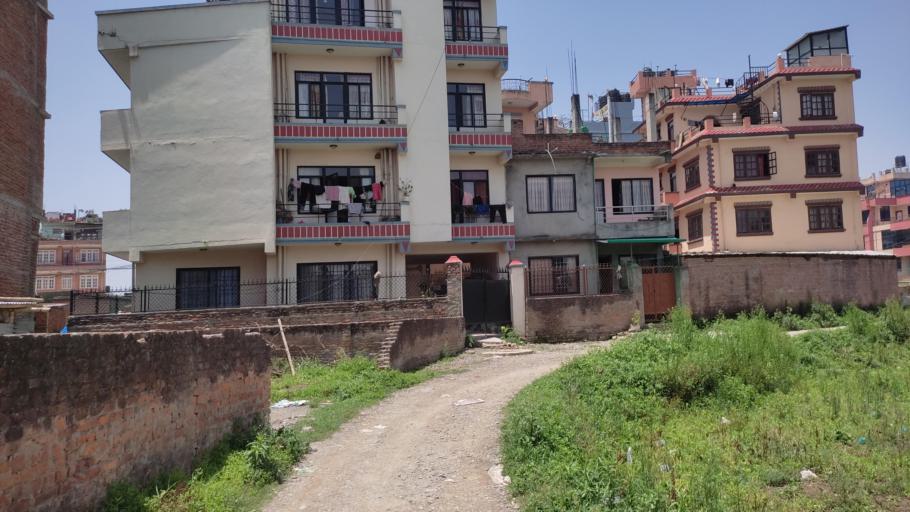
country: NP
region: Central Region
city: Kirtipur
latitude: 27.6738
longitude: 85.2729
